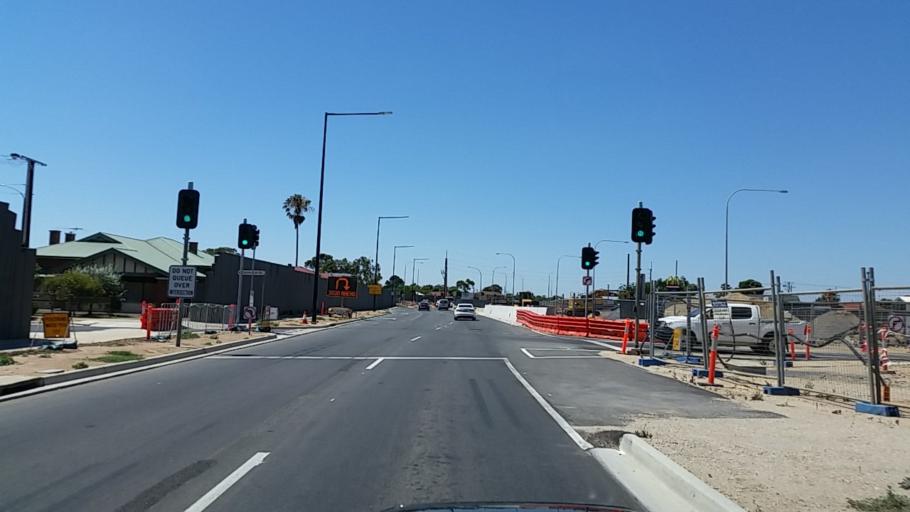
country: AU
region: South Australia
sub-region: Charles Sturt
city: Allenby Gardens
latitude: -34.8903
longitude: 138.5691
